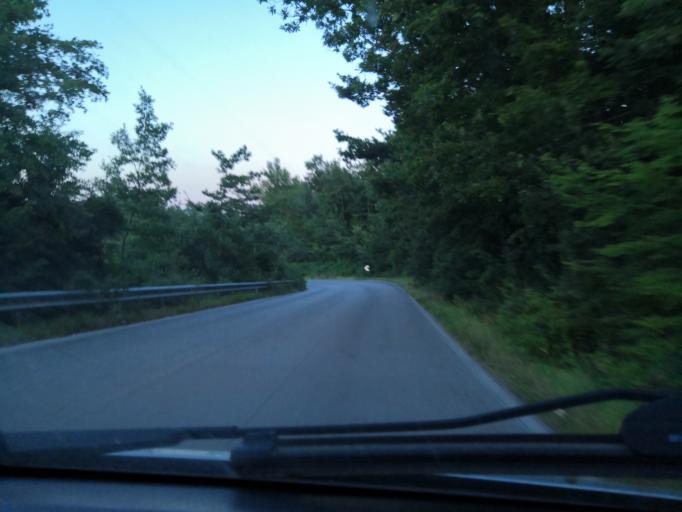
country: IT
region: Molise
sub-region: Provincia di Campobasso
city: Jelsi
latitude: 41.5108
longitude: 14.7819
